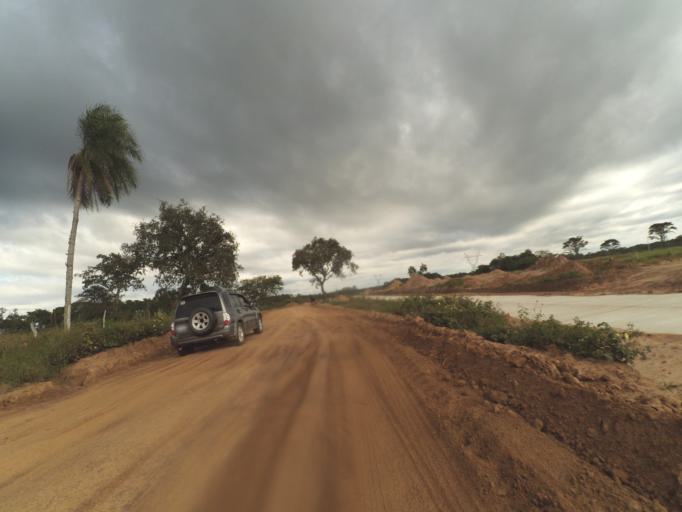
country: BO
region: Santa Cruz
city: Santa Cruz de la Sierra
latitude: -17.7120
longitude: -63.2806
